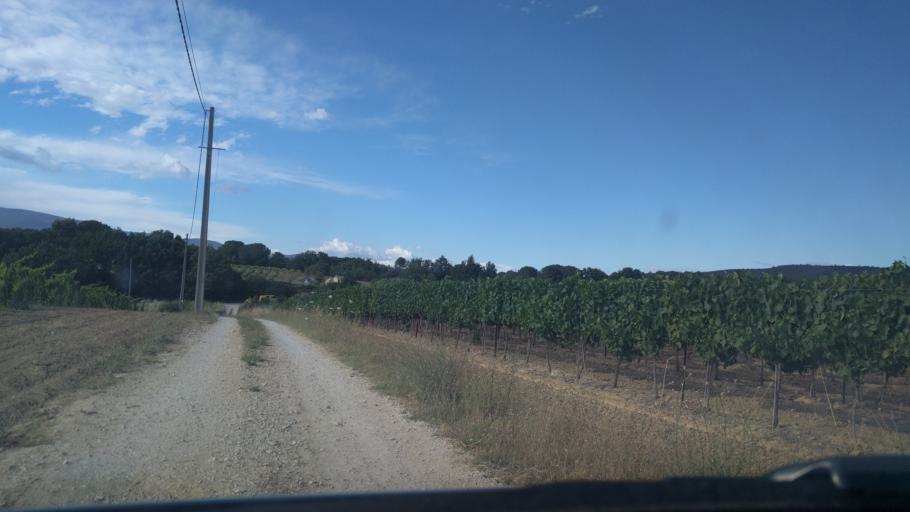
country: FR
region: Provence-Alpes-Cote d'Azur
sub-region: Departement du Vaucluse
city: Grambois
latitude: 43.7296
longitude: 5.5612
